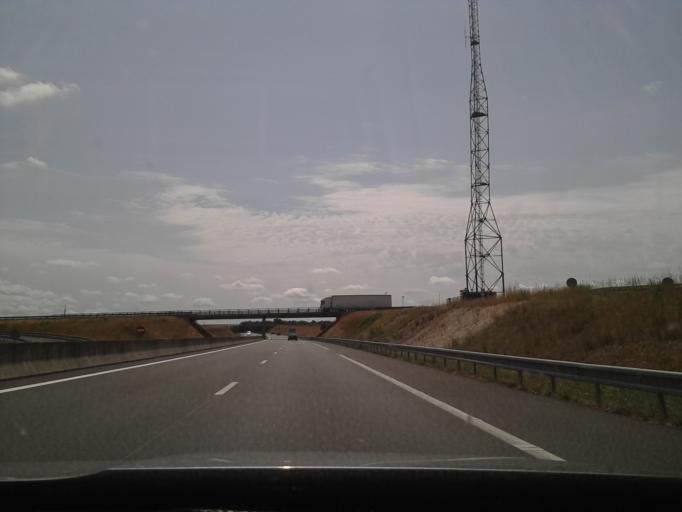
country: FR
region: Centre
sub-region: Departement d'Indre-et-Loire
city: Neuille-Pont-Pierre
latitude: 47.5585
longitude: 0.5937
